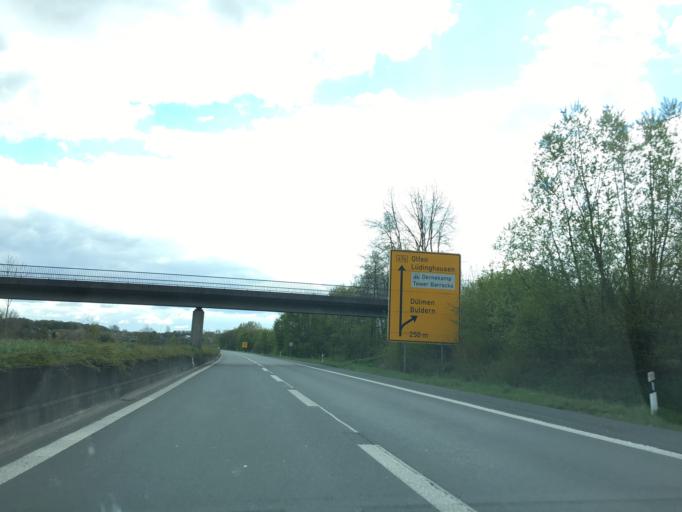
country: DE
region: North Rhine-Westphalia
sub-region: Regierungsbezirk Munster
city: Dulmen
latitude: 51.8499
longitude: 7.2877
